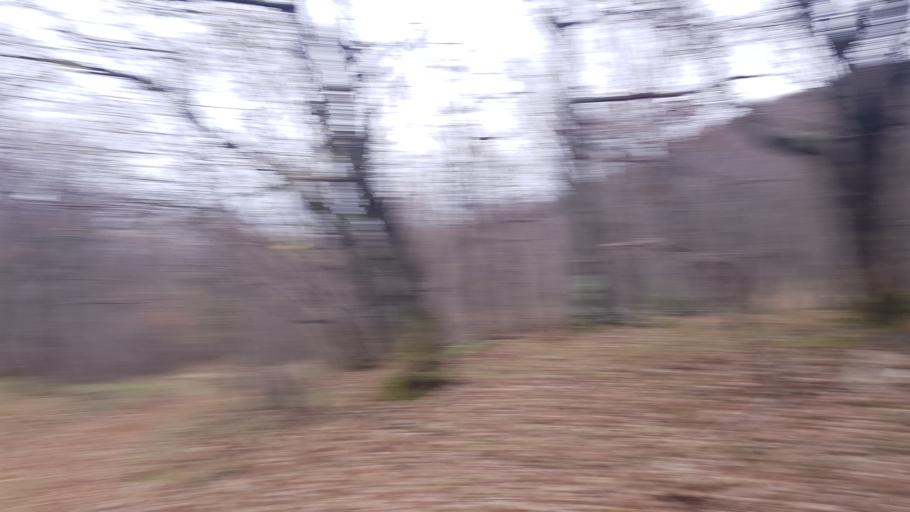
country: IT
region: Friuli Venezia Giulia
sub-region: Provincia di Trieste
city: Zolla
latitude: 45.7387
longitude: 13.7851
